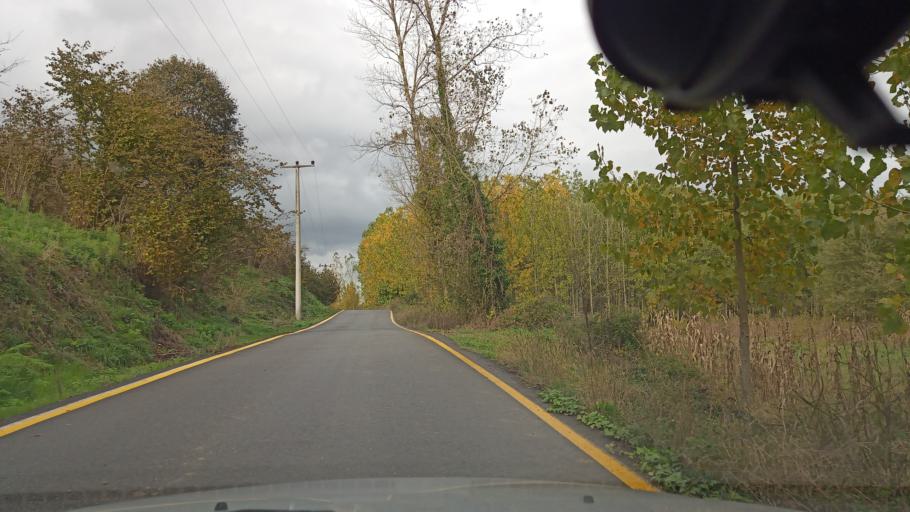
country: TR
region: Sakarya
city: Karasu
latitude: 41.0759
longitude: 30.5973
